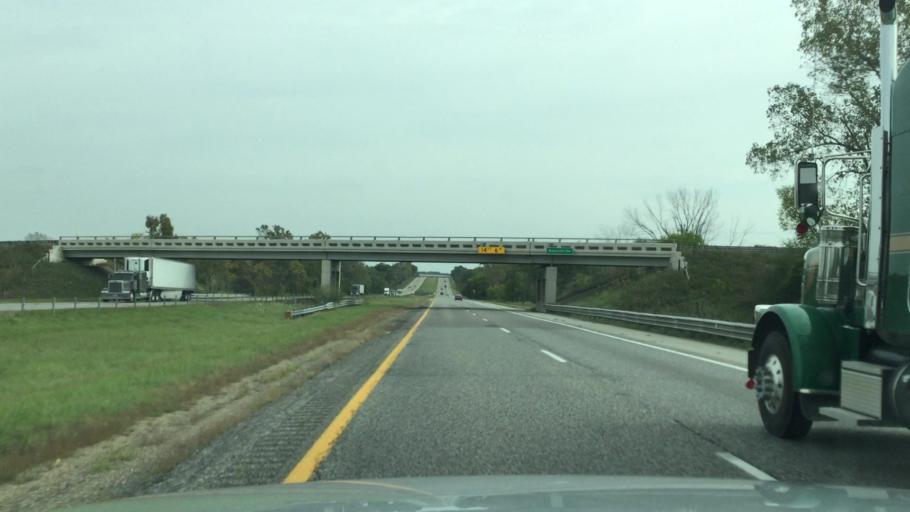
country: US
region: Michigan
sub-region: Shiawassee County
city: Durand
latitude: 42.9028
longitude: -84.0701
